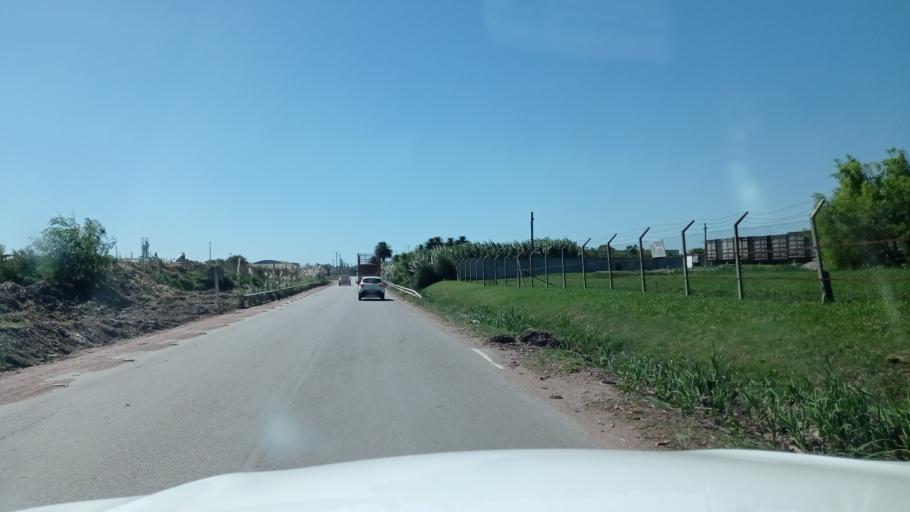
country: UY
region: Montevideo
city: Pajas Blancas
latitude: -34.8682
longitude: -56.2871
